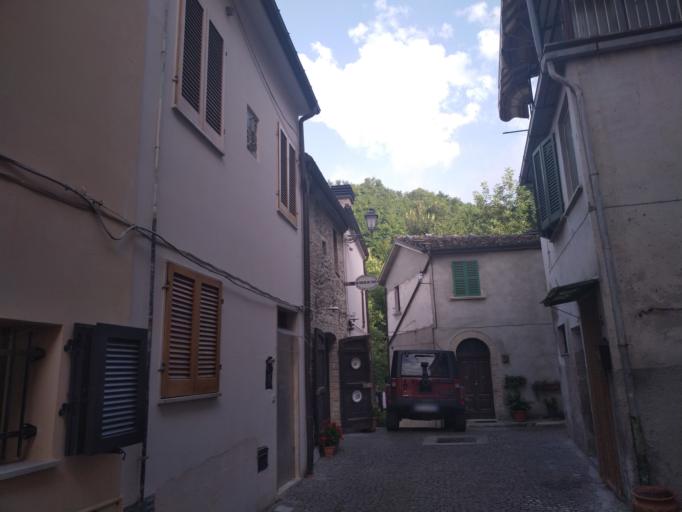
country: IT
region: Abruzzo
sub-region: Provincia di Teramo
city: Castelli
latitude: 42.4887
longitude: 13.7122
